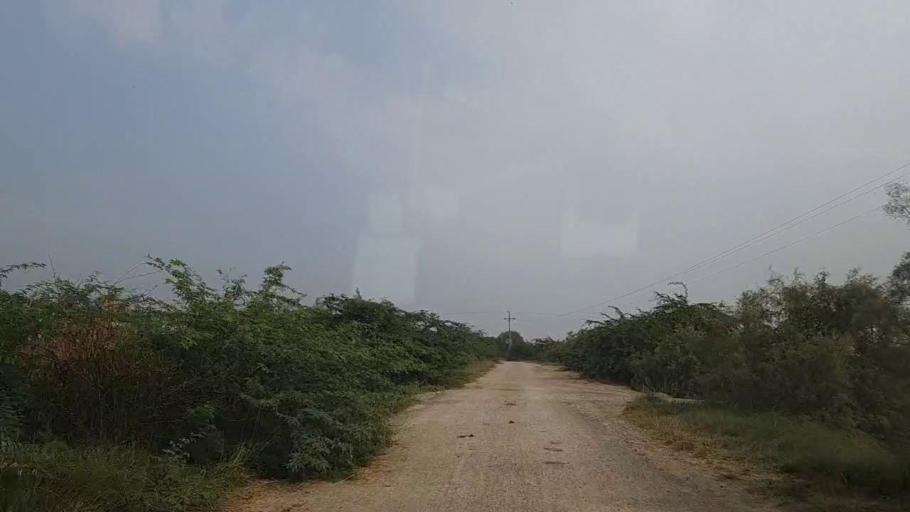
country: PK
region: Sindh
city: Mirpur Sakro
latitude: 24.6150
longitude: 67.7227
